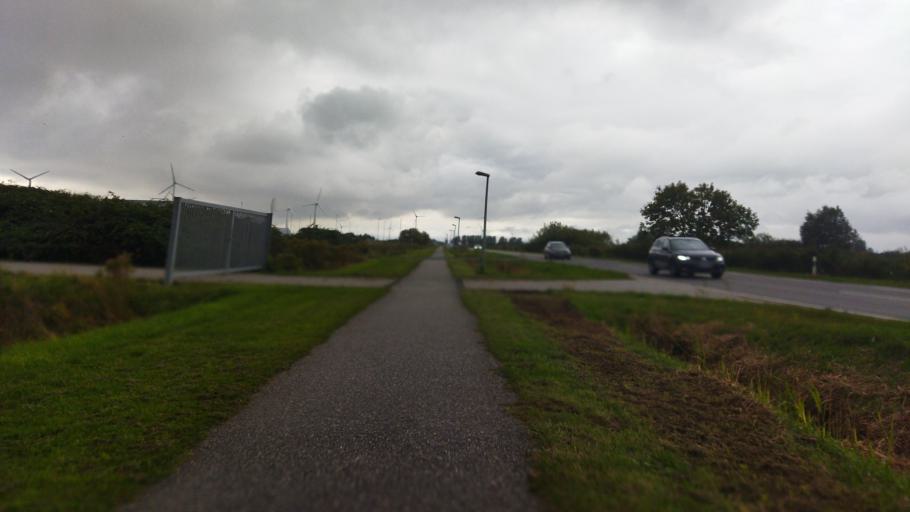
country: DE
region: Lower Saxony
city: Emden
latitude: 53.3604
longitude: 7.1506
